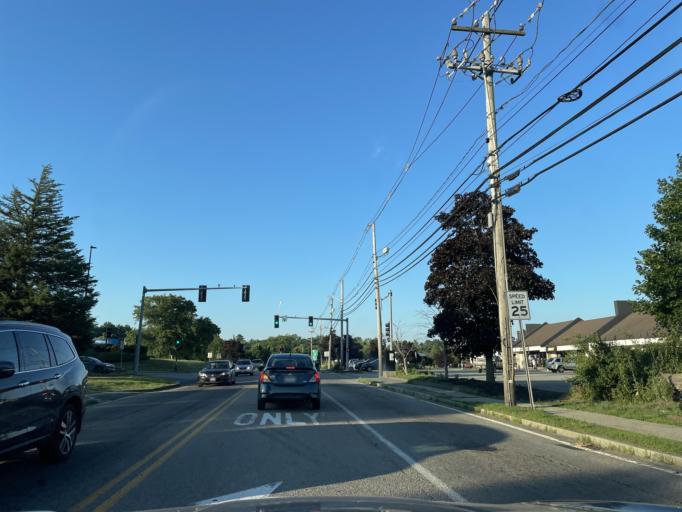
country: US
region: Massachusetts
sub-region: Plymouth County
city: Halifax
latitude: 41.9948
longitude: -70.8456
